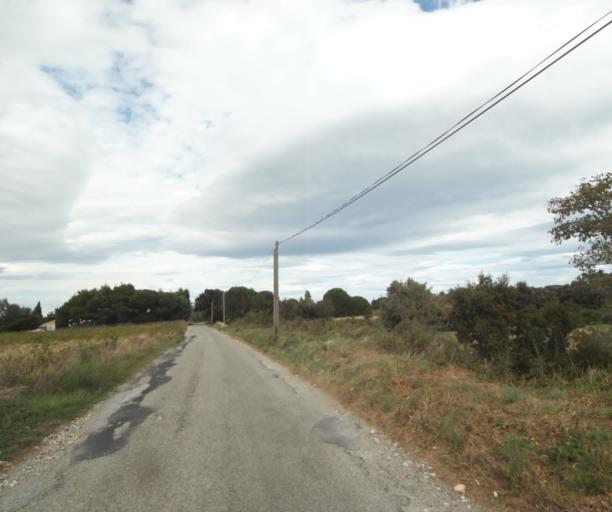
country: FR
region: Languedoc-Roussillon
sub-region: Departement des Pyrenees-Orientales
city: Sant Andreu de Sureda
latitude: 42.5413
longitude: 2.9889
